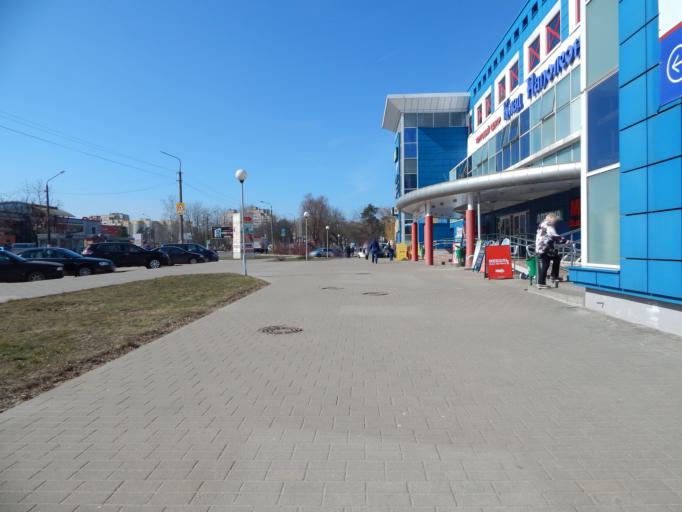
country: BY
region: Minsk
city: Horad Barysaw
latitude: 54.2080
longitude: 28.4909
